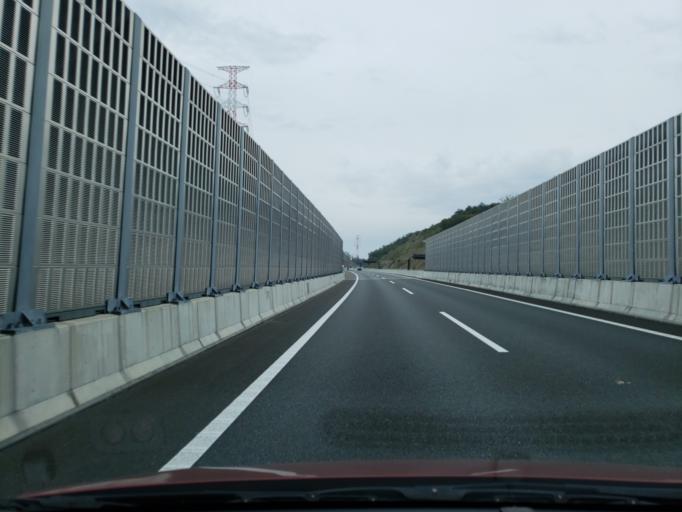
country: JP
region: Hyogo
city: Sandacho
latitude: 34.8578
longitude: 135.2508
